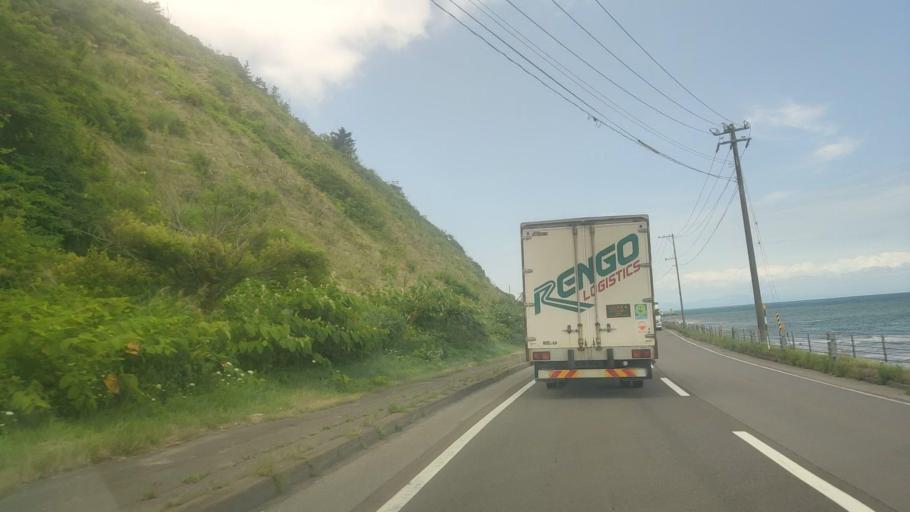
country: JP
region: Hokkaido
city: Nanae
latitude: 42.1519
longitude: 140.4885
